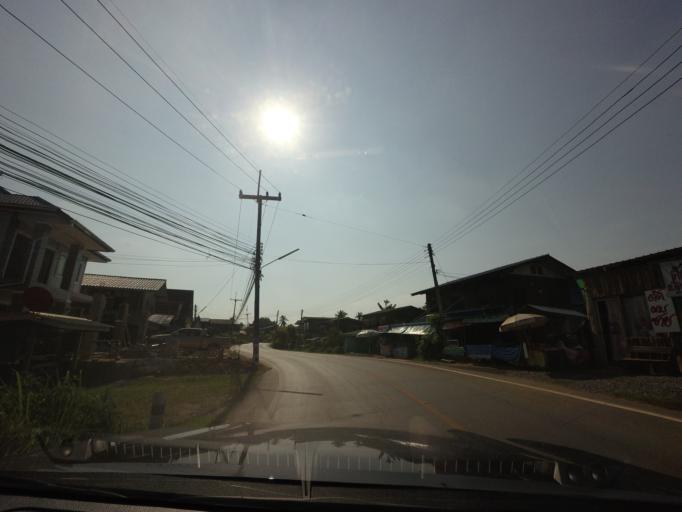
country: TH
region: Nan
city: Nan
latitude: 18.8597
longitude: 100.8193
